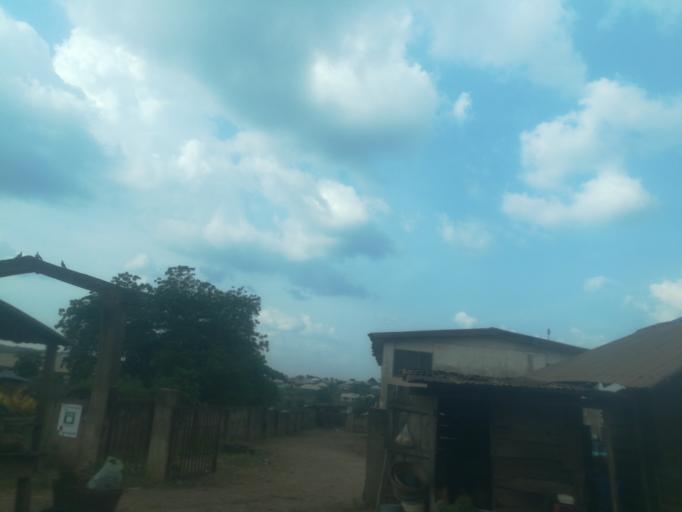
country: NG
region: Ogun
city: Abeokuta
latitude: 7.1364
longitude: 3.2974
